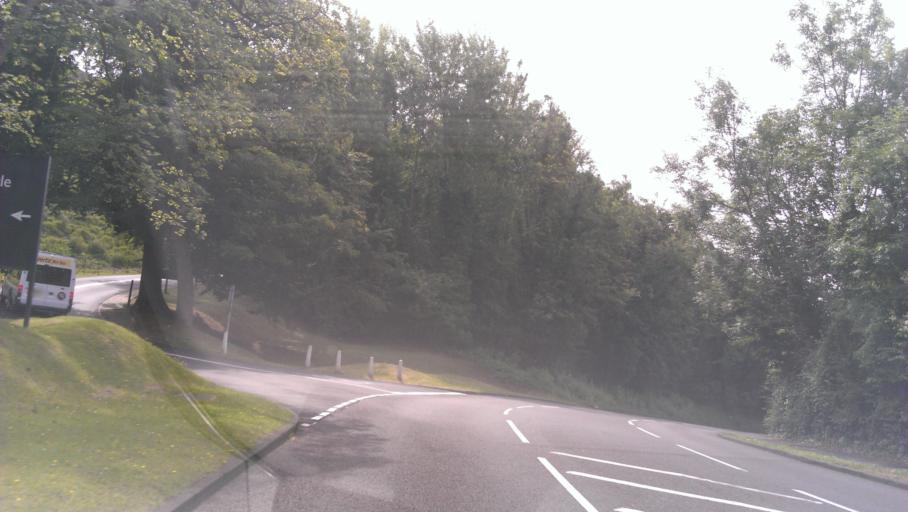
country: GB
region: England
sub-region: Kent
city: Dover
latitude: 51.1282
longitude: 1.3191
